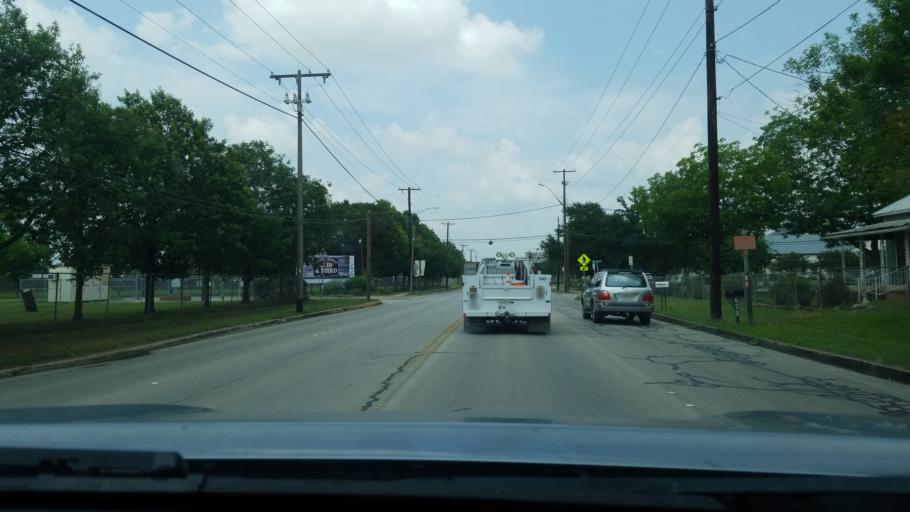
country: US
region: Texas
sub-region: Comal County
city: New Braunfels
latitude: 29.7128
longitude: -98.1142
